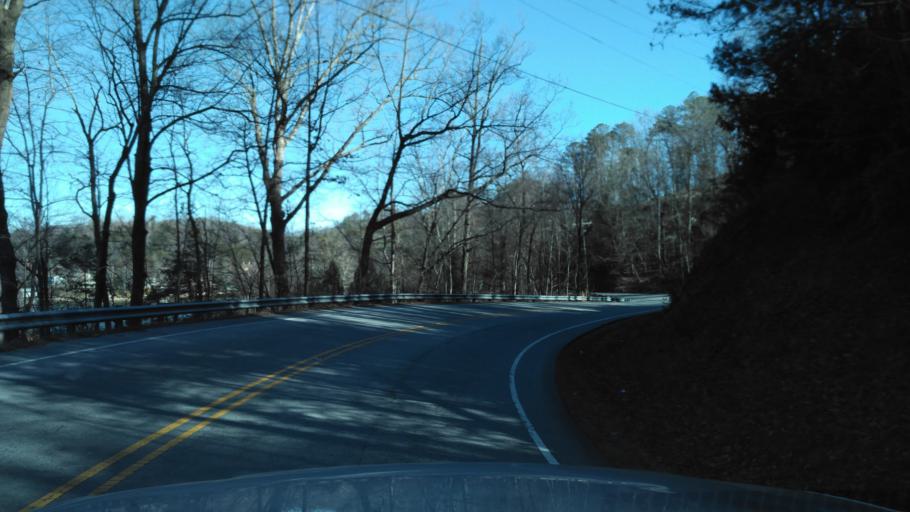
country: US
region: North Carolina
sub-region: Rutherford County
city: Lake Lure
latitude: 35.4204
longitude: -82.1996
